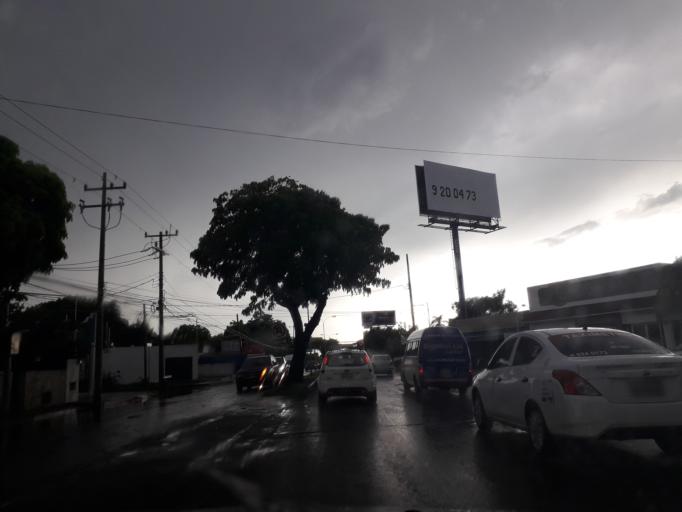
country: MX
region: Yucatan
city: Merida
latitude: 20.9786
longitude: -89.6458
